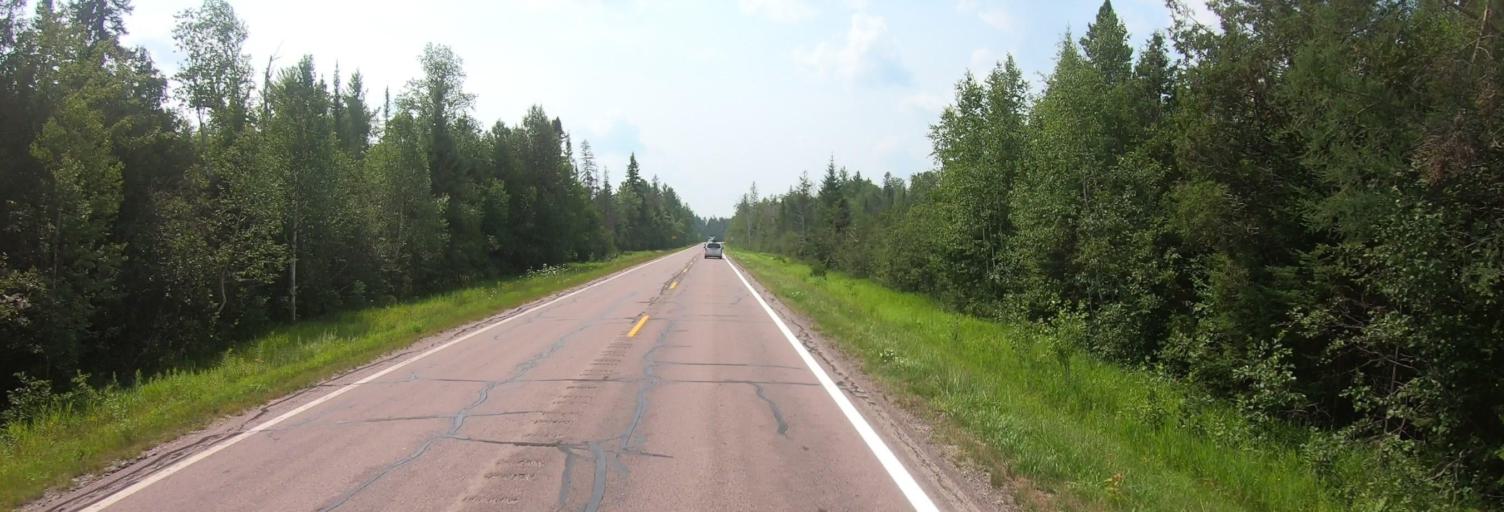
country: US
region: Michigan
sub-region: Luce County
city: Newberry
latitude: 46.4777
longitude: -85.4269
